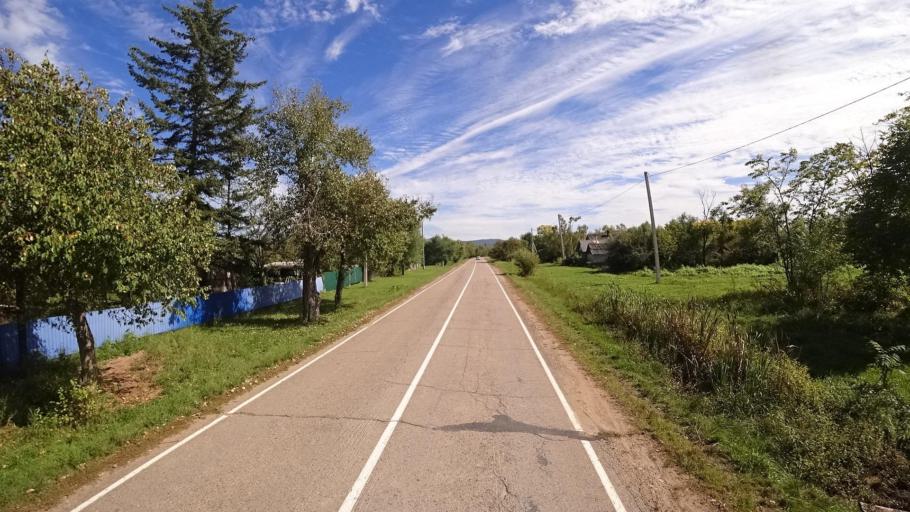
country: RU
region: Primorskiy
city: Yakovlevka
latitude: 44.4287
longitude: 133.5712
